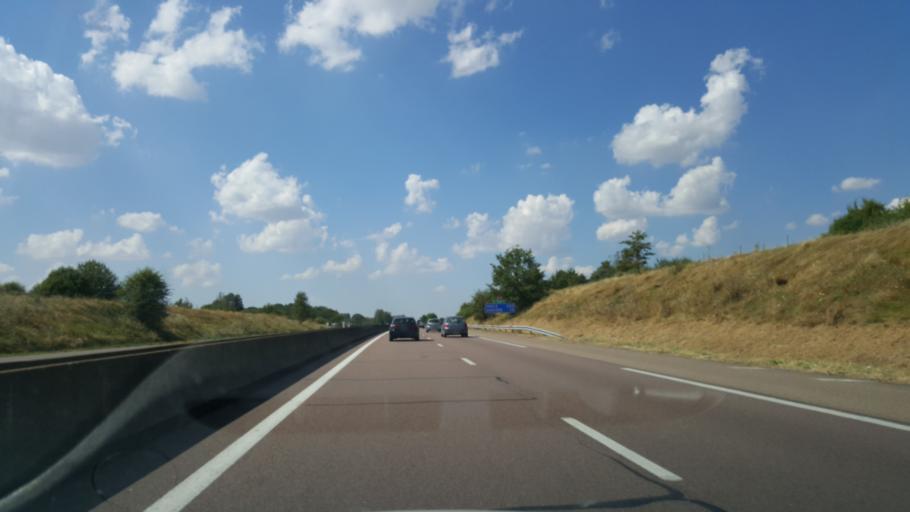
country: FR
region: Bourgogne
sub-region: Departement de la Cote-d'Or
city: Semur-en-Auxois
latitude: 47.4411
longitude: 4.2985
